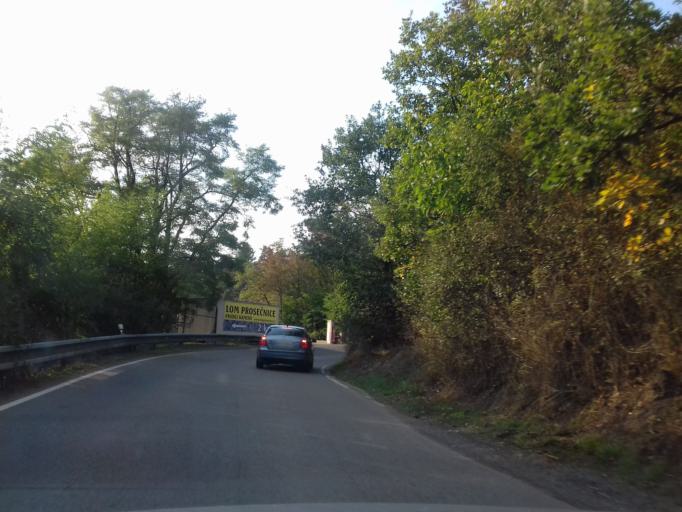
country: CZ
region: Central Bohemia
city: Kamenny Privoz
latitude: 49.8734
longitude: 14.5017
